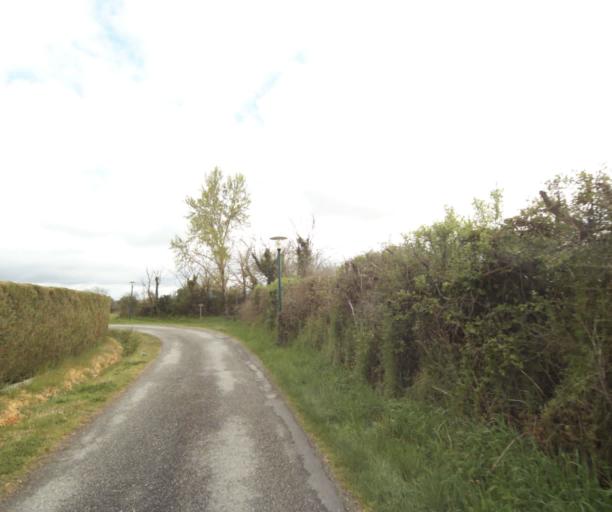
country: FR
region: Midi-Pyrenees
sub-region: Departement de l'Ariege
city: Saverdun
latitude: 43.2360
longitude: 1.5648
